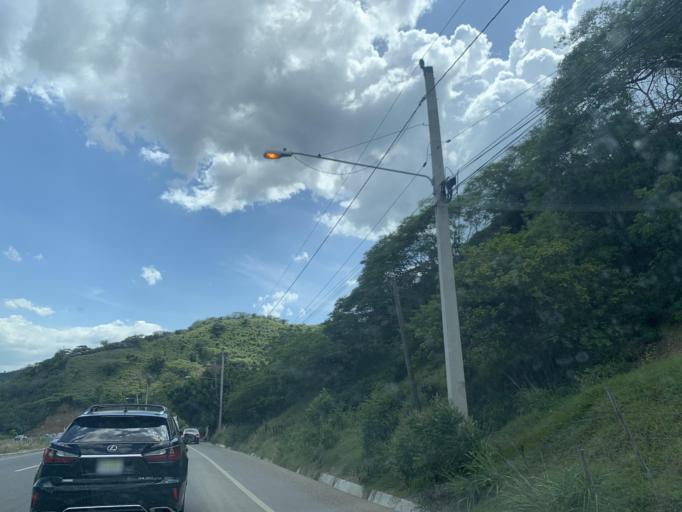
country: DO
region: Santiago
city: Villa Bisono
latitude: 19.5973
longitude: -70.8423
